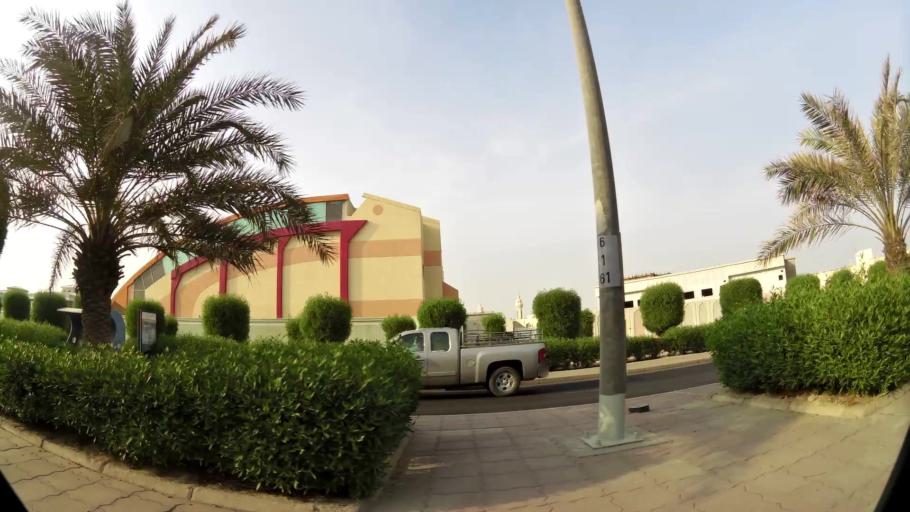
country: KW
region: Mubarak al Kabir
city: Mubarak al Kabir
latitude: 29.1839
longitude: 48.0791
